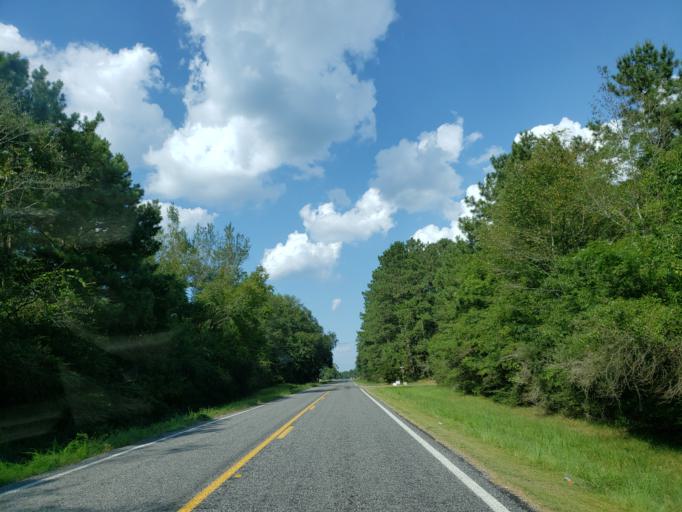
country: US
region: Mississippi
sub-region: Covington County
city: Collins
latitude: 31.6076
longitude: -89.4355
